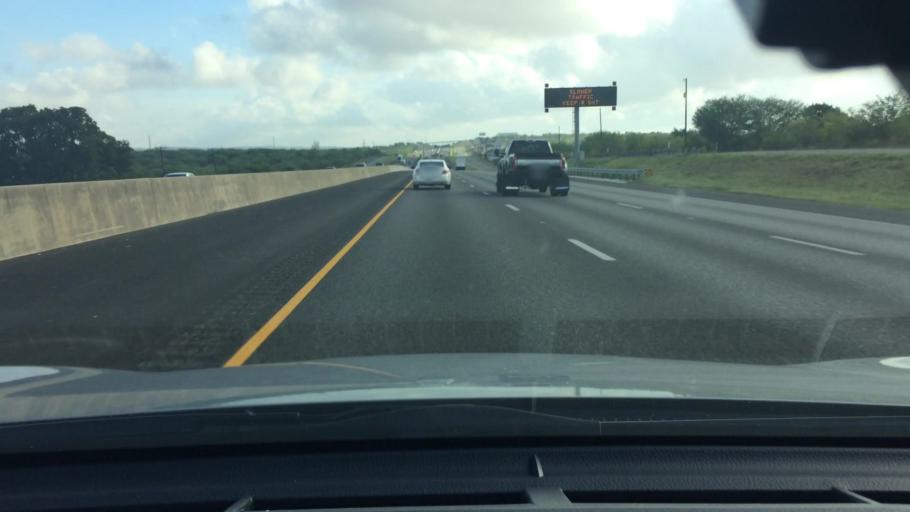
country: US
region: Texas
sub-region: Guadalupe County
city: Lake Dunlap
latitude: 29.7637
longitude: -98.0453
